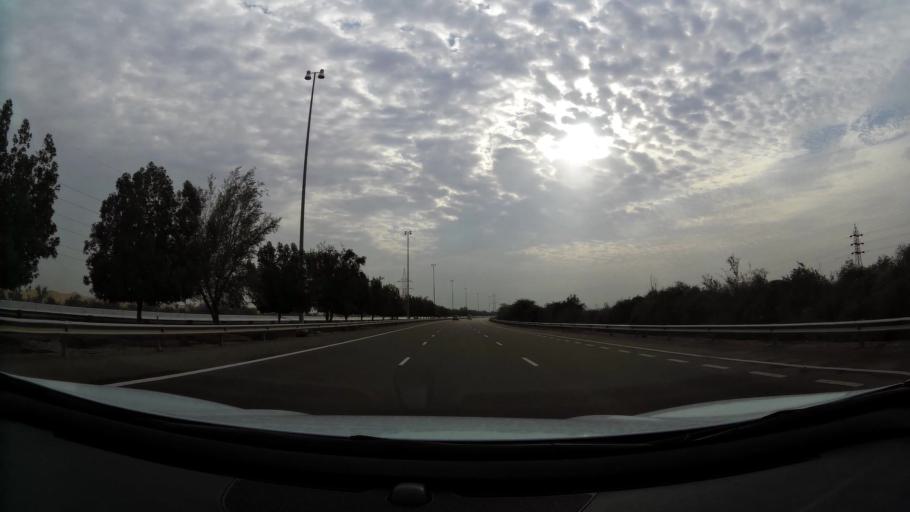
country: AE
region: Abu Dhabi
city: Al Ain
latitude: 24.1800
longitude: 55.0478
